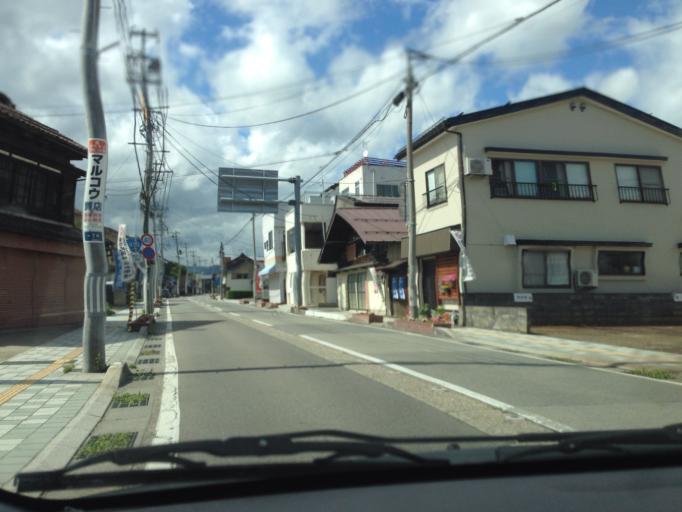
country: JP
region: Fukushima
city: Kitakata
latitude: 37.6550
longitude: 139.8728
